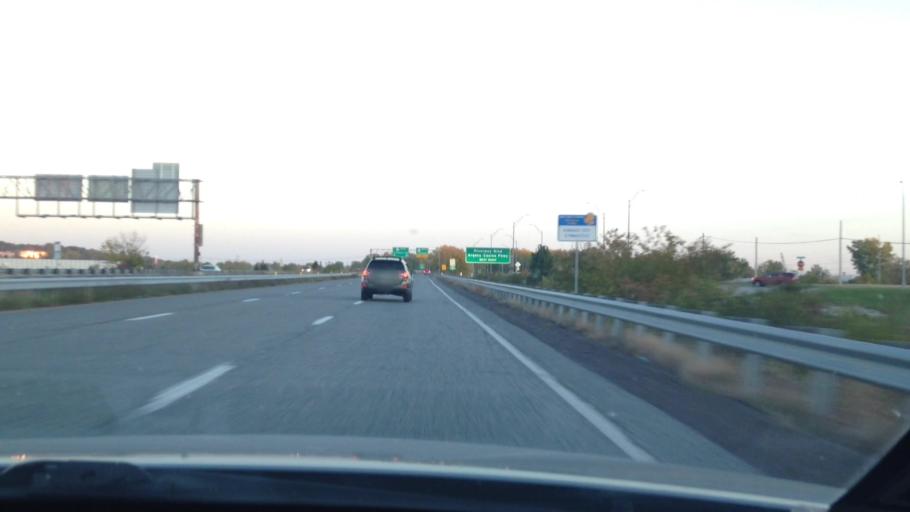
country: US
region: Missouri
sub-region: Platte County
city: Riverside
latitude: 39.1692
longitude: -94.6188
